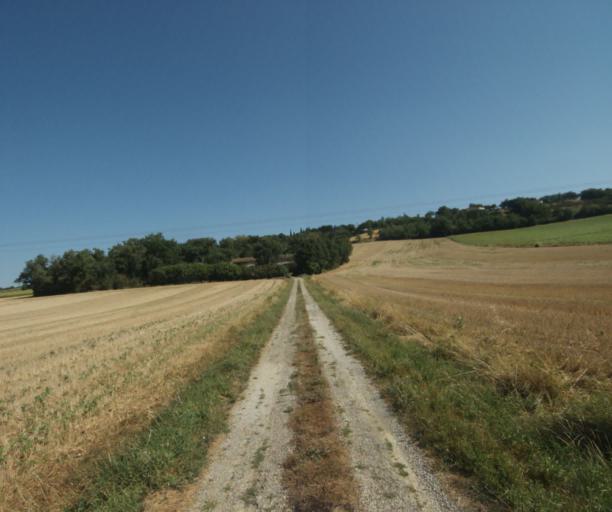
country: FR
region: Midi-Pyrenees
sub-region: Departement de la Haute-Garonne
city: Saint-Felix-Lauragais
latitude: 43.5127
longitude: 1.9181
